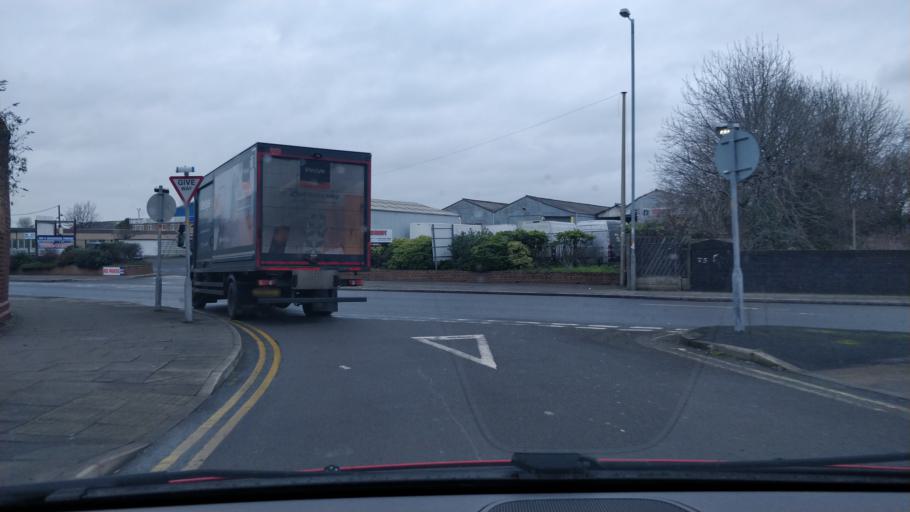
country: GB
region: England
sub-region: Sefton
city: Litherland
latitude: 53.4565
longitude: -2.9842
